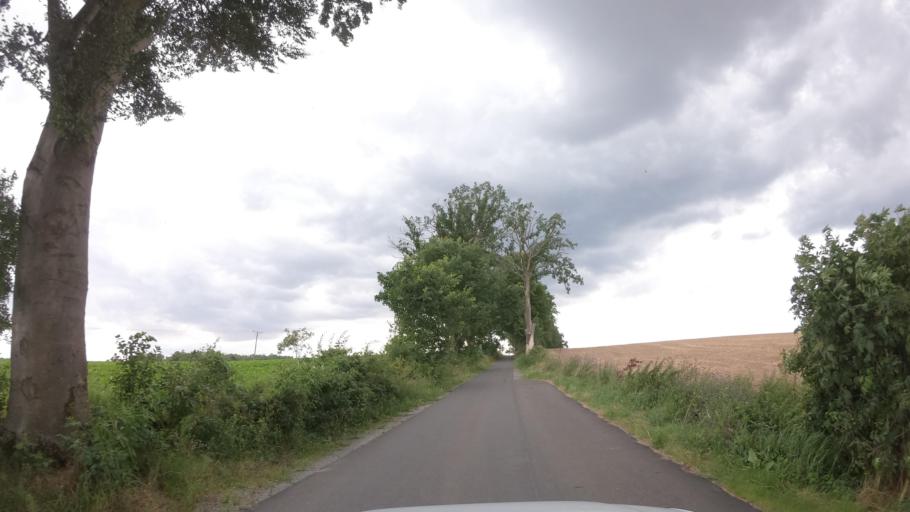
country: PL
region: West Pomeranian Voivodeship
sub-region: Powiat stargardzki
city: Suchan
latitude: 53.1863
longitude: 15.3117
